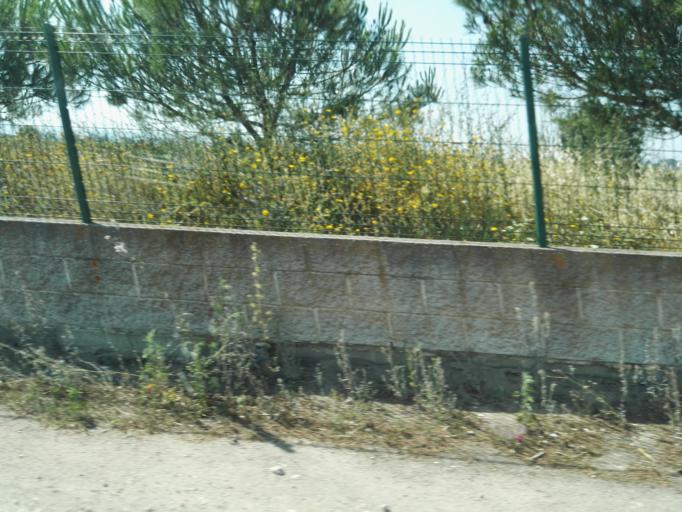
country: PT
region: Santarem
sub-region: Benavente
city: Samora Correia
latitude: 38.9301
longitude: -8.8837
